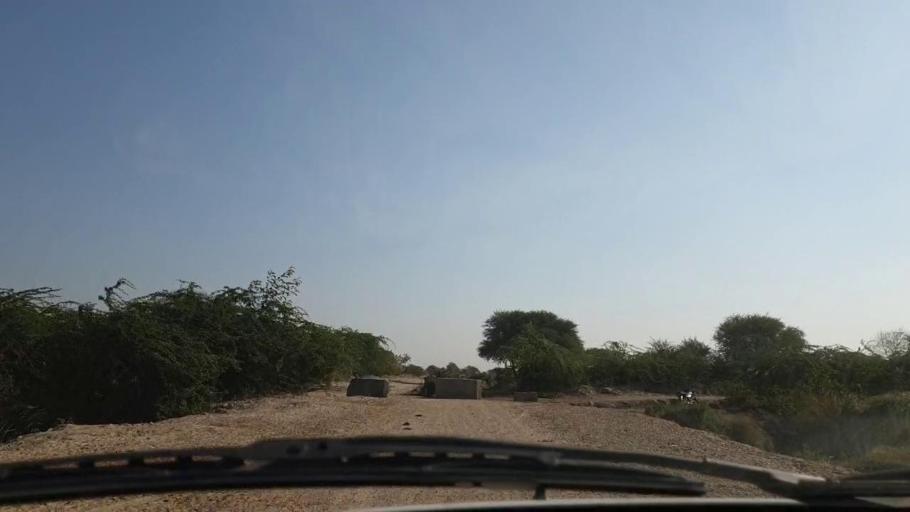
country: PK
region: Sindh
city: Bulri
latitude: 24.7951
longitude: 68.3956
